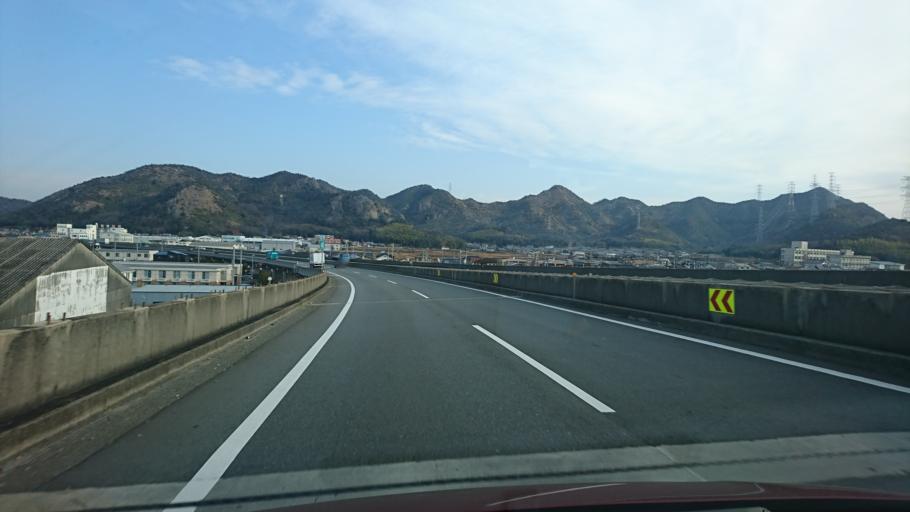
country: JP
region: Hyogo
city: Shirahamacho-usazakiminami
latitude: 34.8132
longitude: 134.7469
